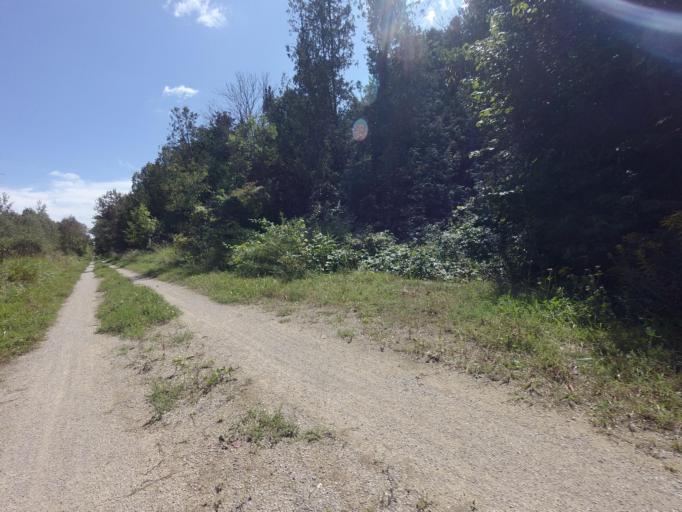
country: CA
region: Ontario
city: Orangeville
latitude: 43.7773
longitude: -80.2052
